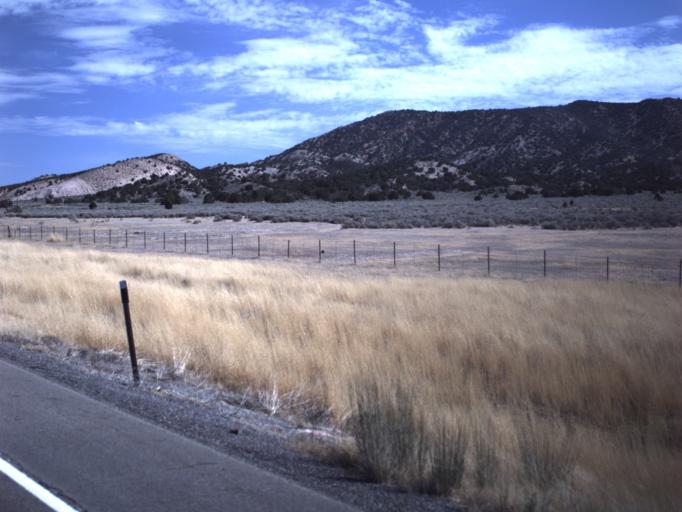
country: US
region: Utah
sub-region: Sanpete County
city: Gunnison
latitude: 39.3952
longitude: -111.9279
